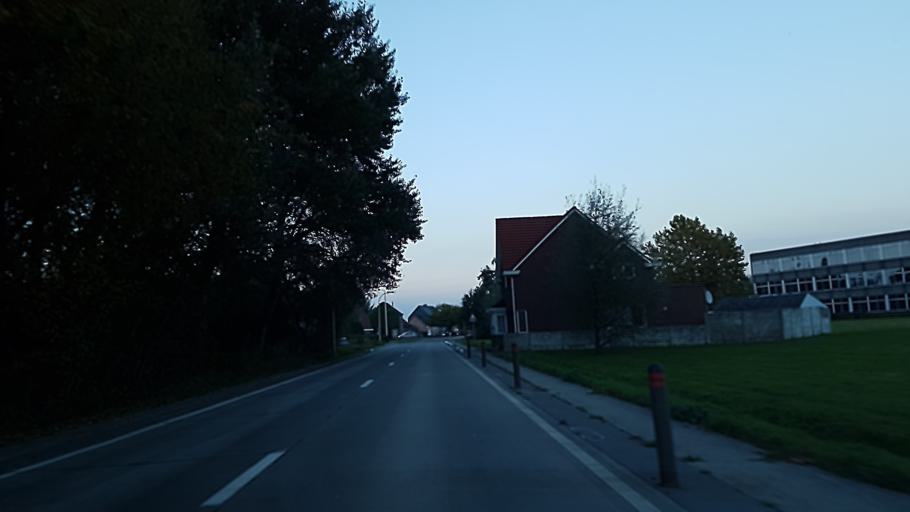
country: BE
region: Flanders
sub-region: Provincie Antwerpen
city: Duffel
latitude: 51.0862
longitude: 4.4795
